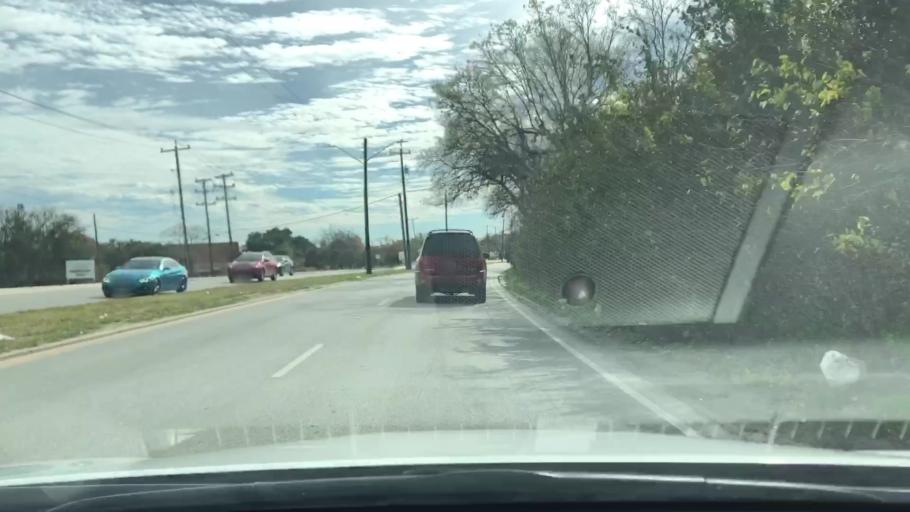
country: US
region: Texas
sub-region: Bexar County
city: Terrell Hills
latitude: 29.5132
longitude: -98.4359
